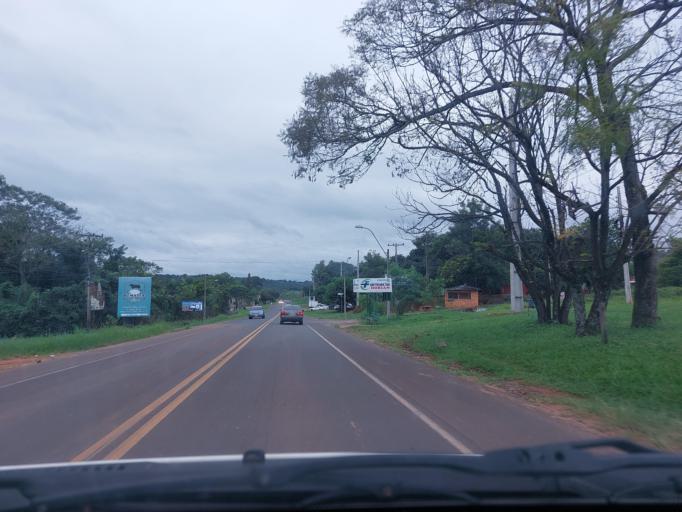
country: PY
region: San Pedro
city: Guayaybi
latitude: -24.6634
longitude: -56.4190
